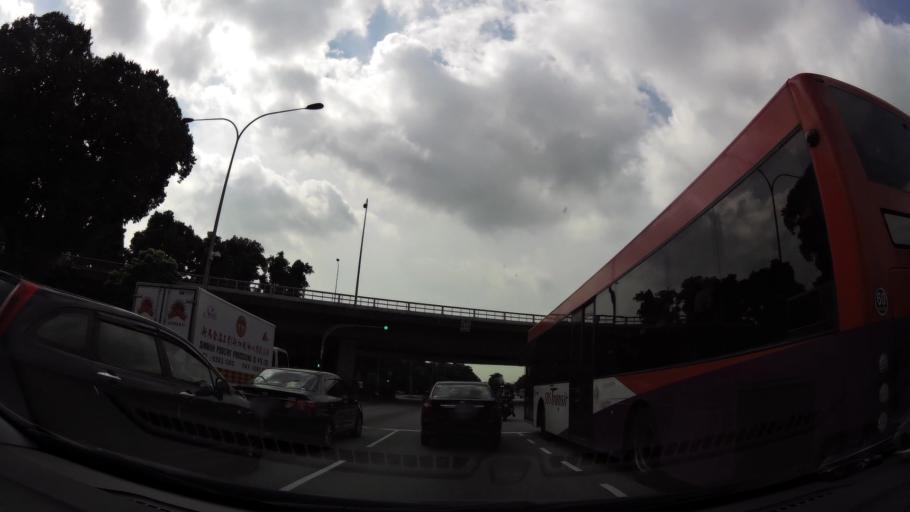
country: SG
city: Singapore
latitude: 1.3267
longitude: 103.9059
